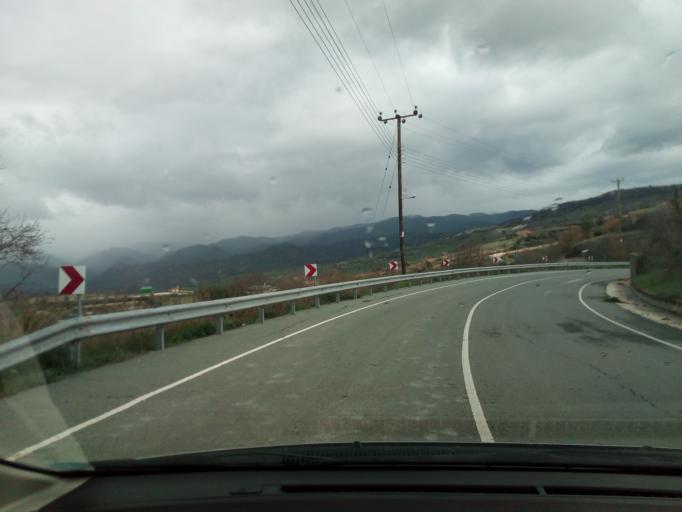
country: CY
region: Pafos
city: Tala
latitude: 34.9328
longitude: 32.5122
